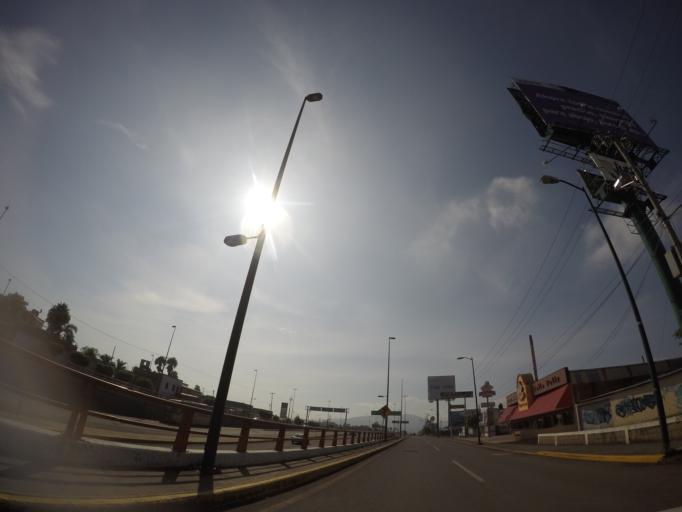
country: MX
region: Michoacan
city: Morelia
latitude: 19.7227
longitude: -101.1918
